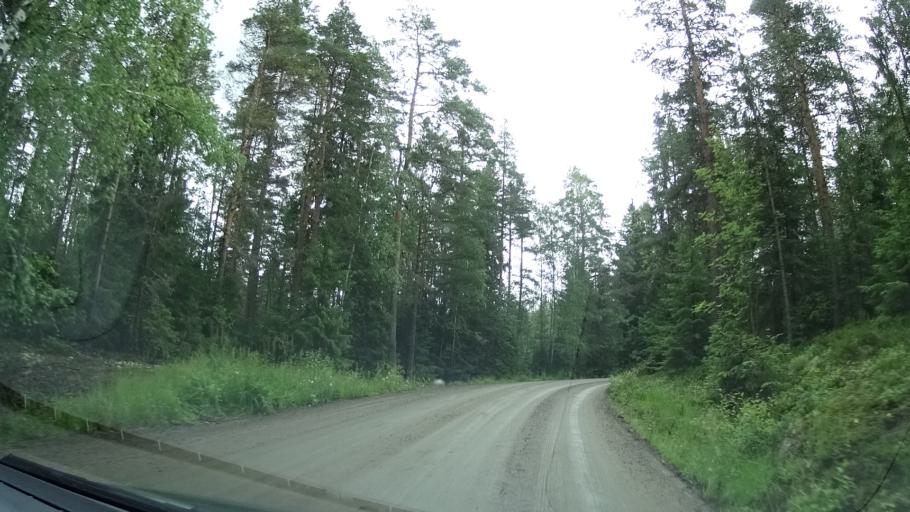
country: FI
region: Pirkanmaa
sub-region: Lounais-Pirkanmaa
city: Punkalaidun
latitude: 61.1040
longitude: 23.2787
